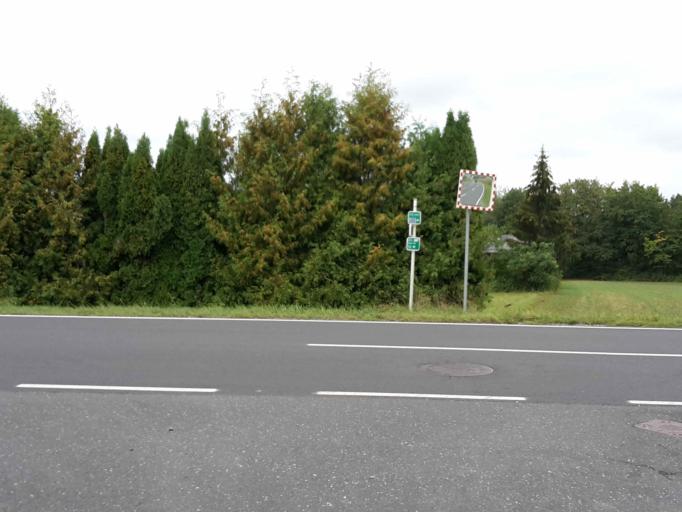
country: AT
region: Carinthia
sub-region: Politischer Bezirk Volkermarkt
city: Eberndorf
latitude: 46.6201
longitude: 14.6086
